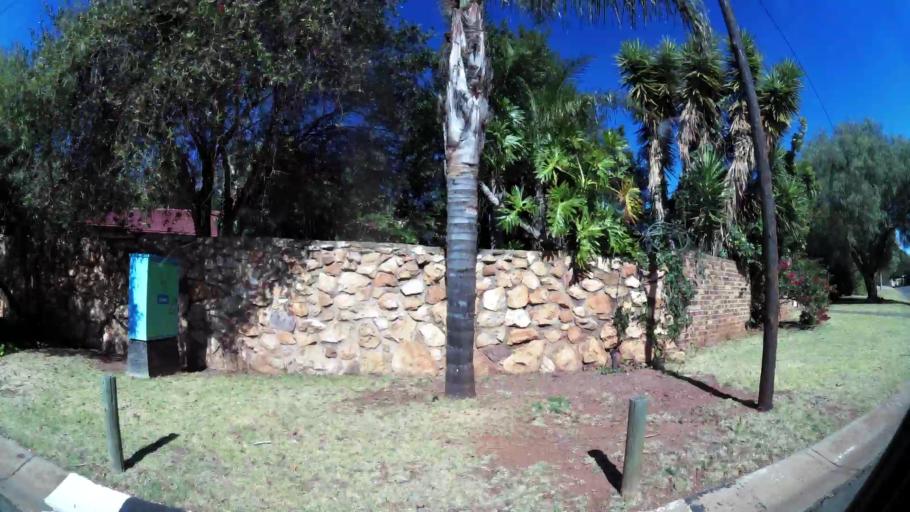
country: ZA
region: Gauteng
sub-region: City of Johannesburg Metropolitan Municipality
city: Roodepoort
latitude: -26.1162
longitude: 27.8550
